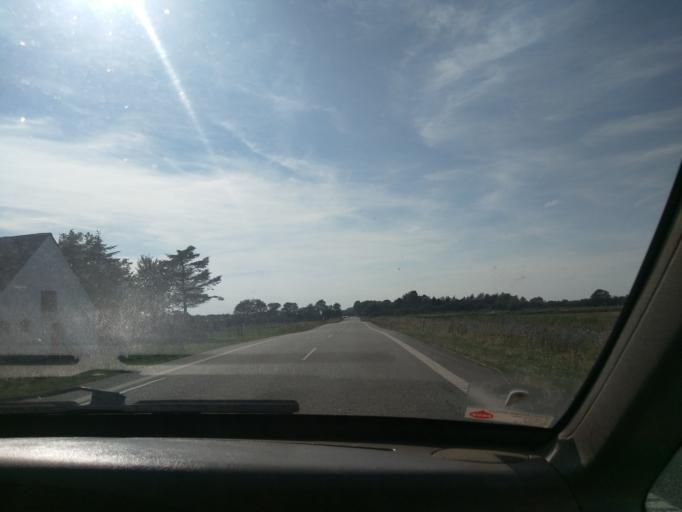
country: DK
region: Central Jutland
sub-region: Viborg Kommune
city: Bjerringbro
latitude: 56.4355
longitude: 9.6796
